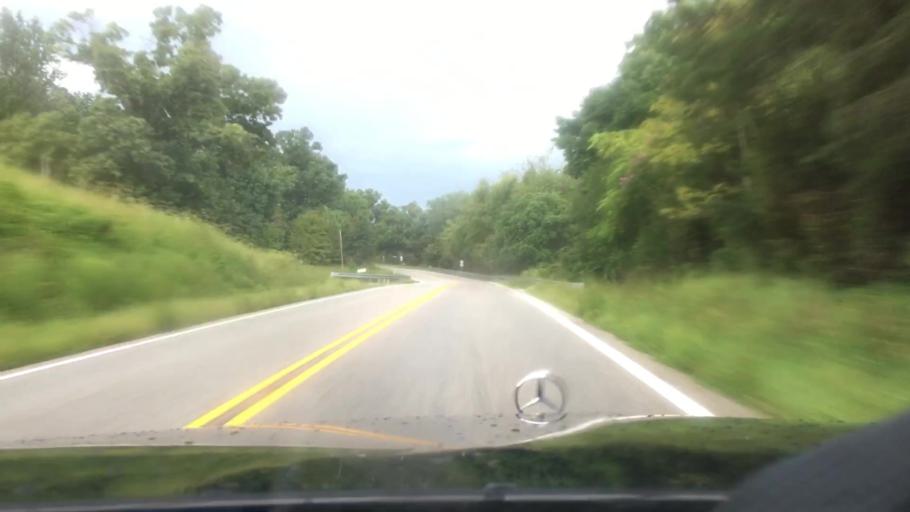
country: US
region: Virginia
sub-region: Nelson County
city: Lovingston
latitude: 37.7746
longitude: -78.9818
